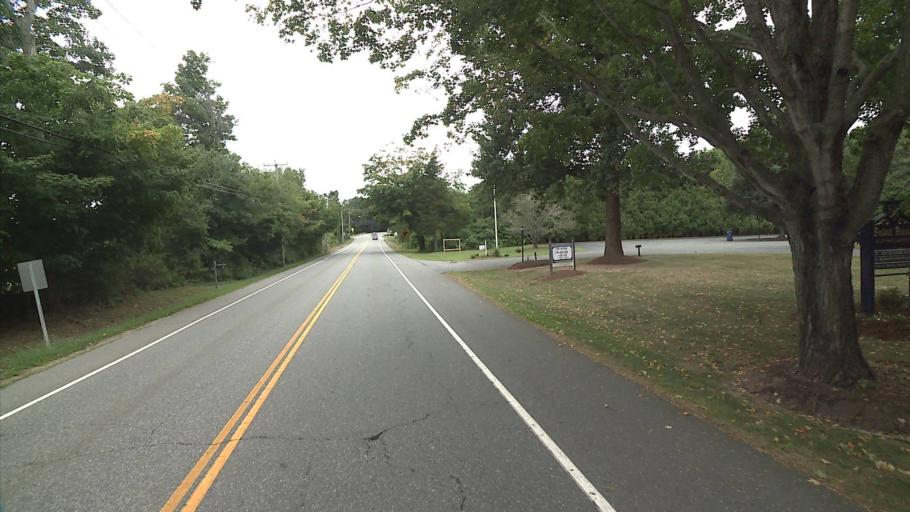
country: US
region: Connecticut
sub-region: Middlesex County
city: Old Saybrook Center
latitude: 41.2970
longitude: -72.3203
